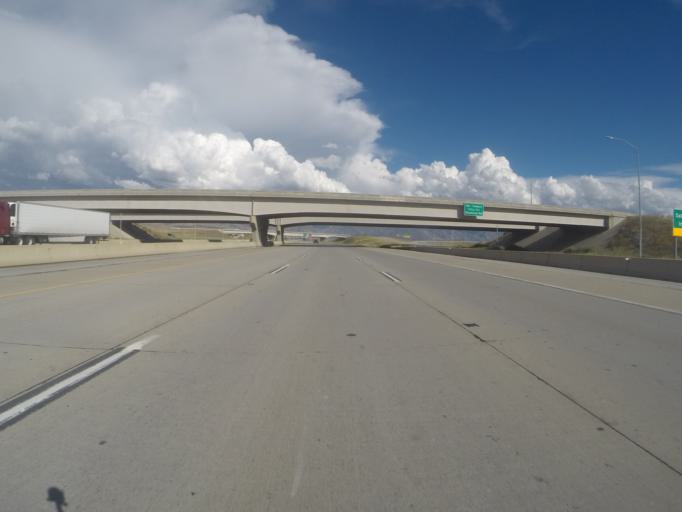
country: US
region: Utah
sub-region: Salt Lake County
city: West Valley City
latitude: 40.7644
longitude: -111.9880
